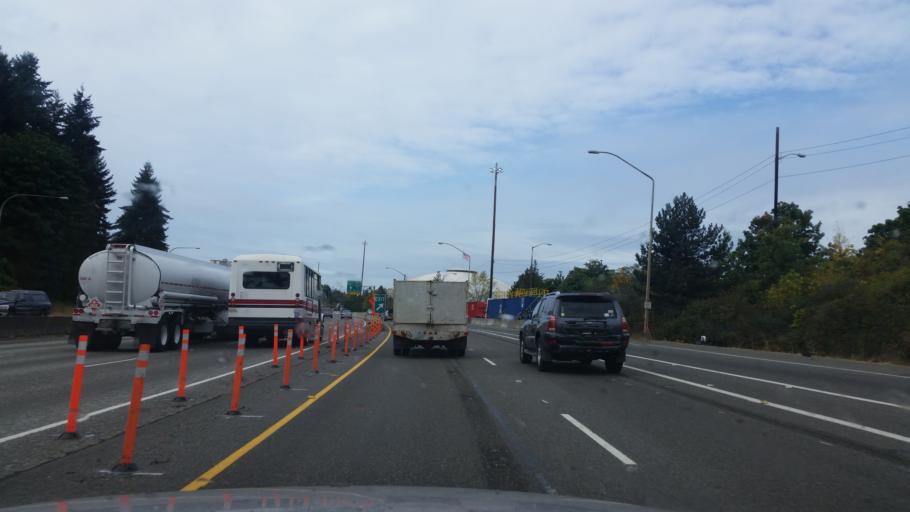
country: US
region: Washington
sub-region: Pierce County
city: Tacoma
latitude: 47.2384
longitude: -122.4183
